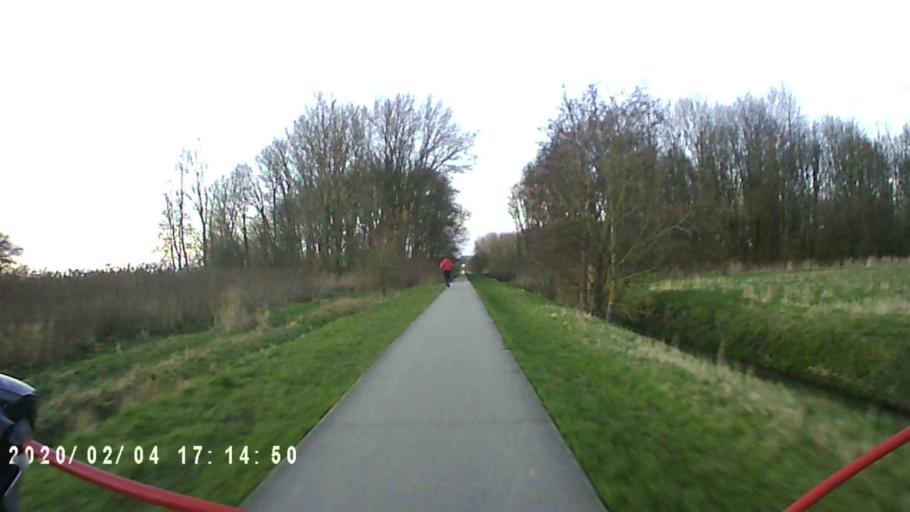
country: NL
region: Groningen
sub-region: Gemeente Groningen
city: Korrewegwijk
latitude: 53.2467
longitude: 6.5231
